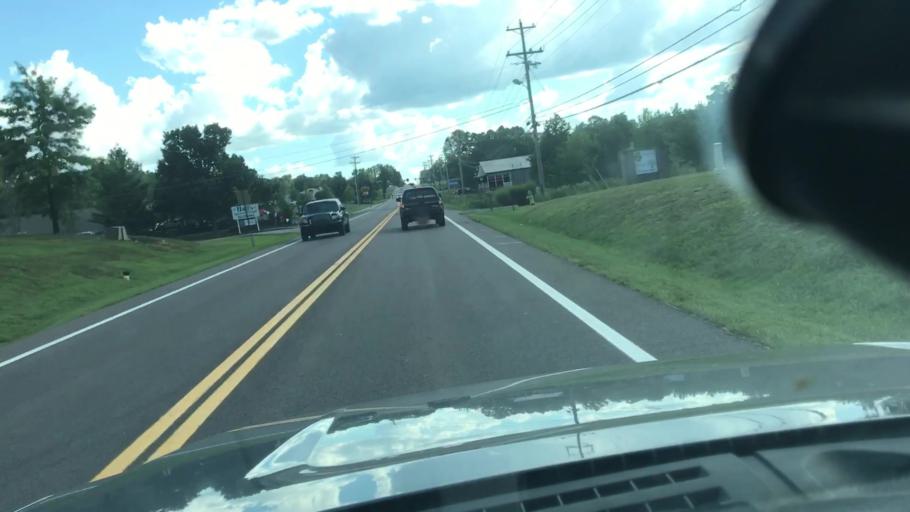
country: US
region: Tennessee
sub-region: Williamson County
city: Fairview
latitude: 35.9647
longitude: -87.1341
